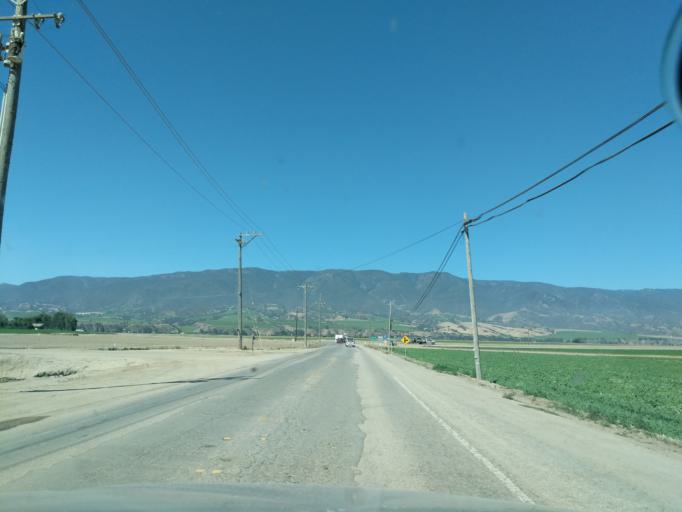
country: US
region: California
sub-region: Monterey County
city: Soledad
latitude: 36.3961
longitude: -121.3315
